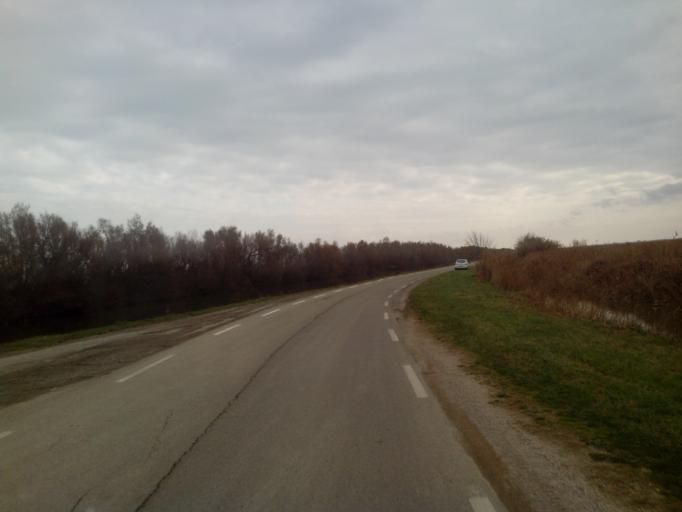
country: FR
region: Languedoc-Roussillon
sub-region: Departement du Gard
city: Vauvert
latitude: 43.6365
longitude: 4.2996
